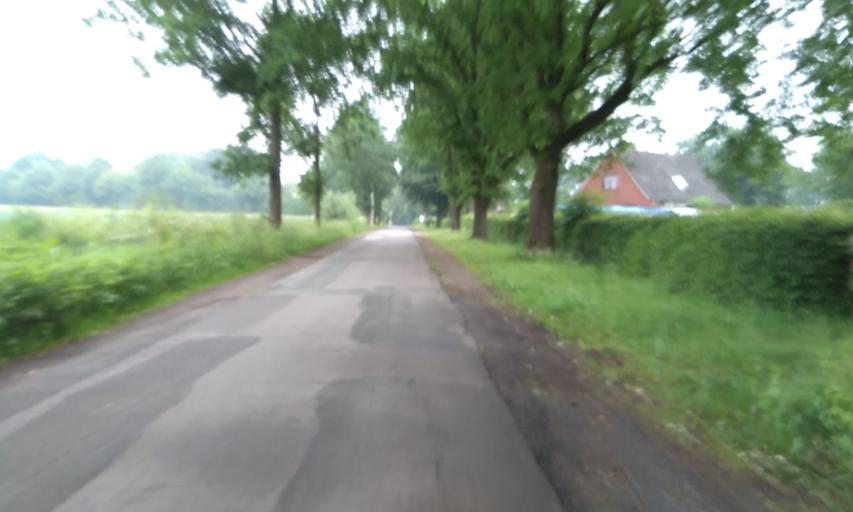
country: DE
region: Lower Saxony
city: Deinste
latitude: 53.5422
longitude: 9.4327
